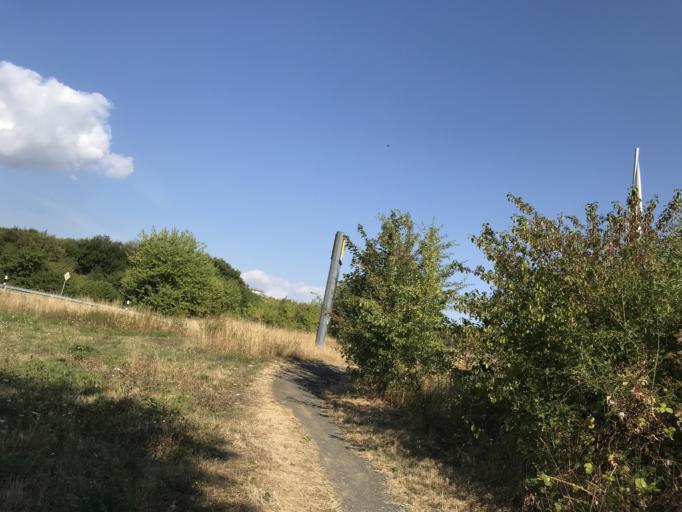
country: DE
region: Hesse
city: Staufenberg
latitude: 50.6546
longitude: 8.7328
